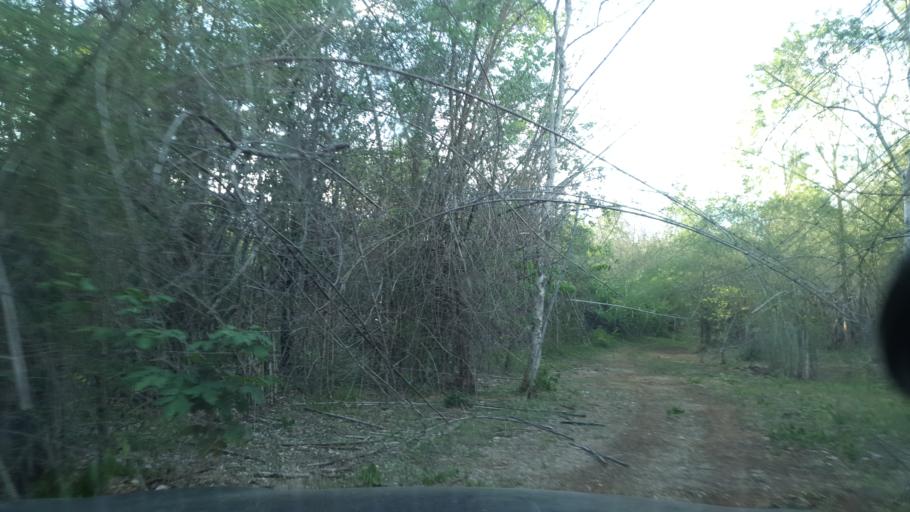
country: TH
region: Lampang
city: Sop Prap
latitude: 17.9654
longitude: 99.3512
